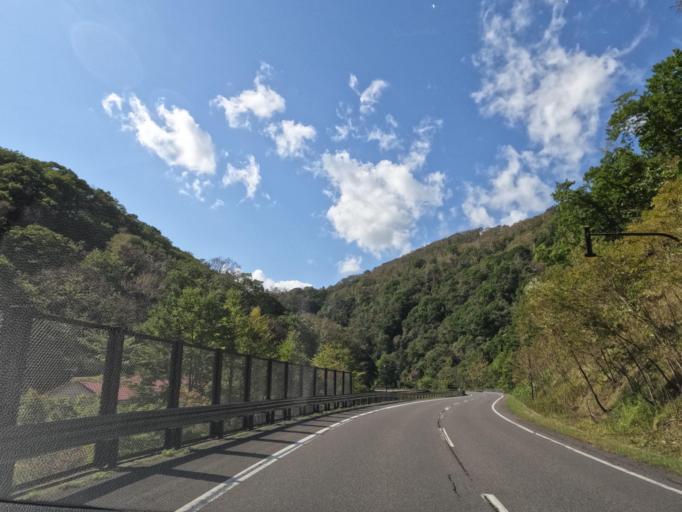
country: JP
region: Hokkaido
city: Shiraoi
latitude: 42.4865
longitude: 141.1473
